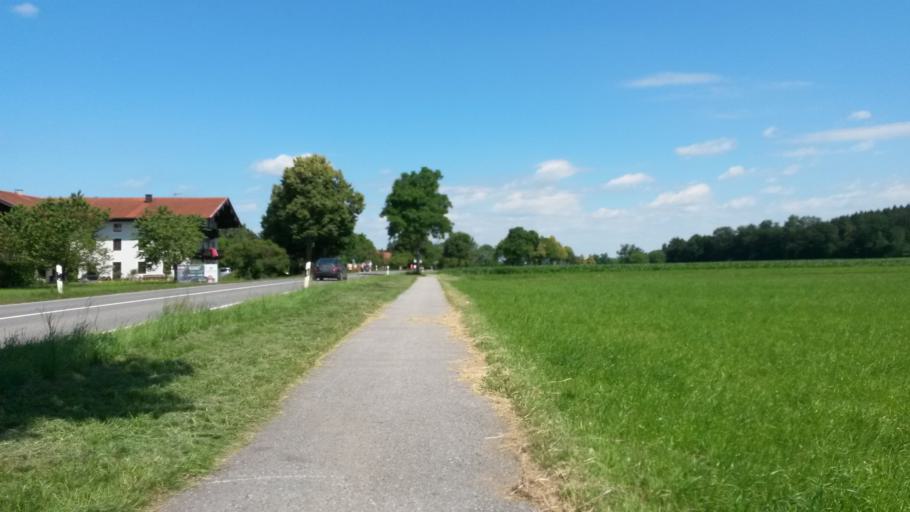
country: DE
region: Bavaria
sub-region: Upper Bavaria
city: Chieming
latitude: 47.8717
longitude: 12.5291
